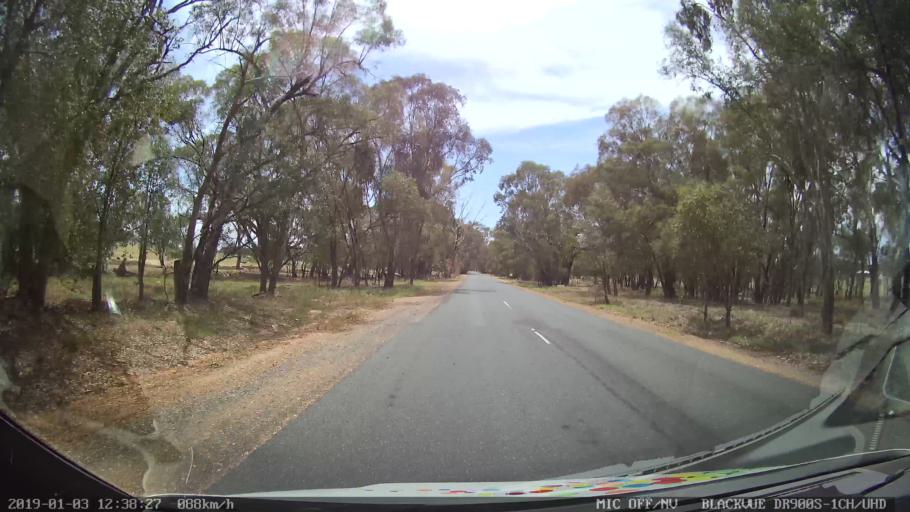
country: AU
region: New South Wales
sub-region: Weddin
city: Grenfell
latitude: -33.8333
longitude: 148.1958
